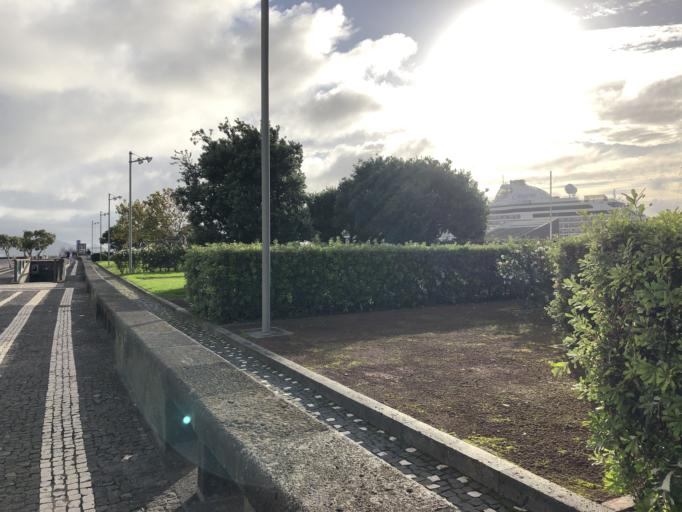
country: PT
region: Azores
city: Ponta Delgada
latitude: 37.7400
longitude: -25.6644
